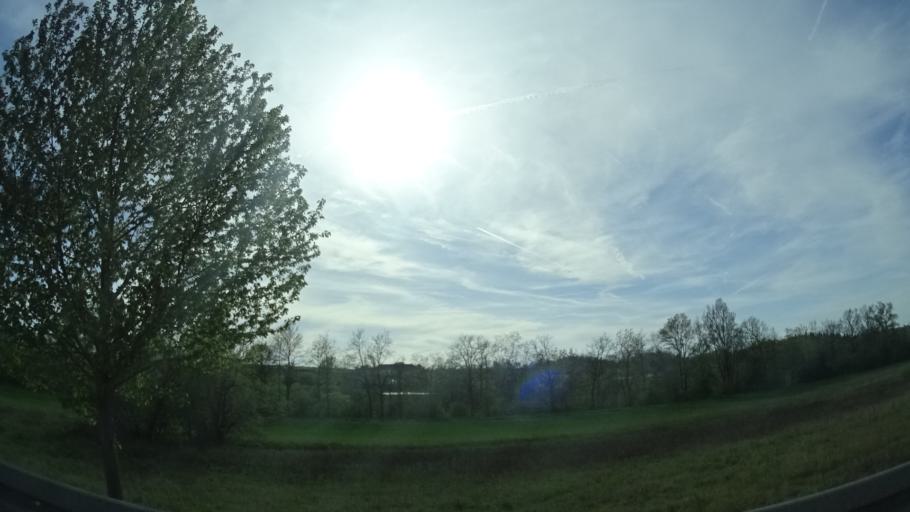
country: DE
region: Bavaria
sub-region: Regierungsbezirk Unterfranken
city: Volkach
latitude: 49.8499
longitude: 10.2289
